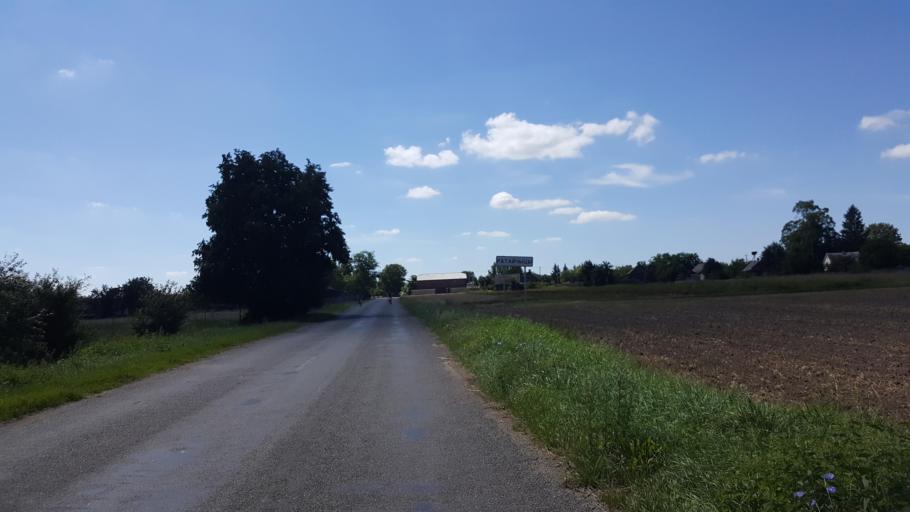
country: BY
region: Brest
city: Charnawchytsy
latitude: 52.3478
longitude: 23.6139
